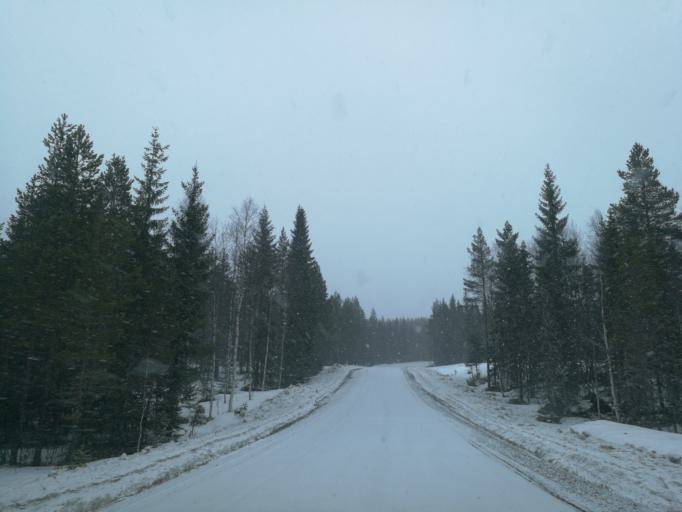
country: SE
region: Vaermland
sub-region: Torsby Kommun
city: Torsby
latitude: 60.6492
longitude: 12.8979
